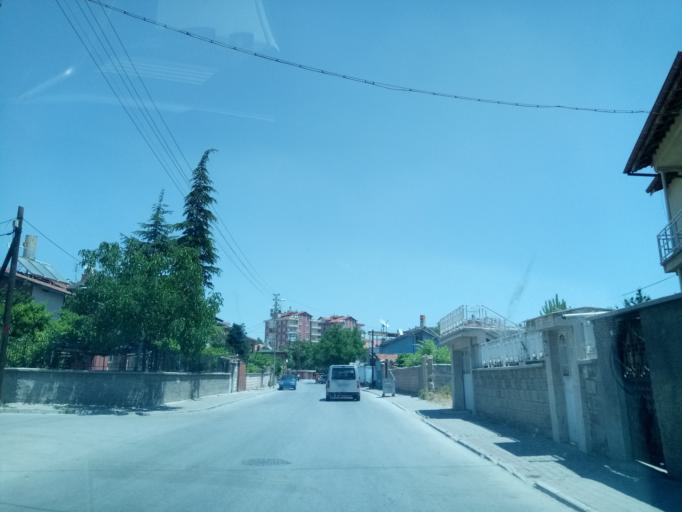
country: TR
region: Konya
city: Konya
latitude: 37.8473
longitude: 32.4981
